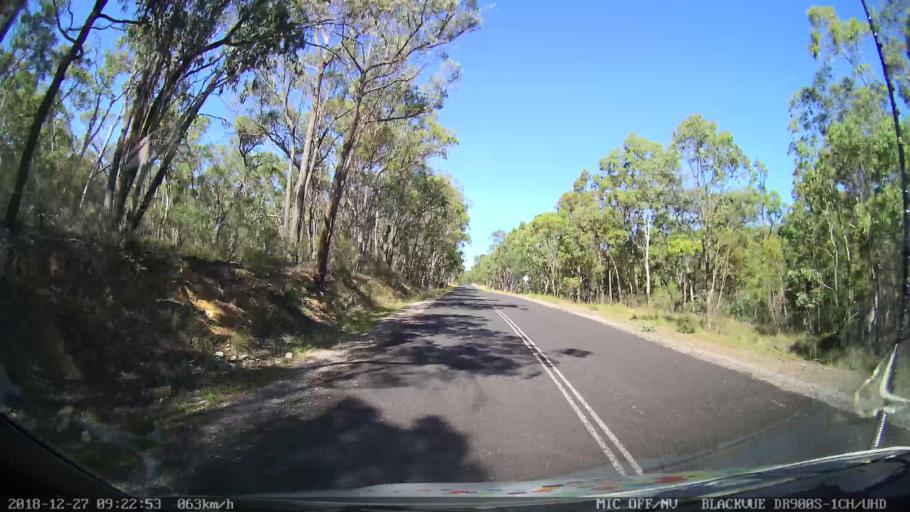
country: AU
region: New South Wales
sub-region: Lithgow
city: Portland
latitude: -33.1236
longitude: 150.0032
